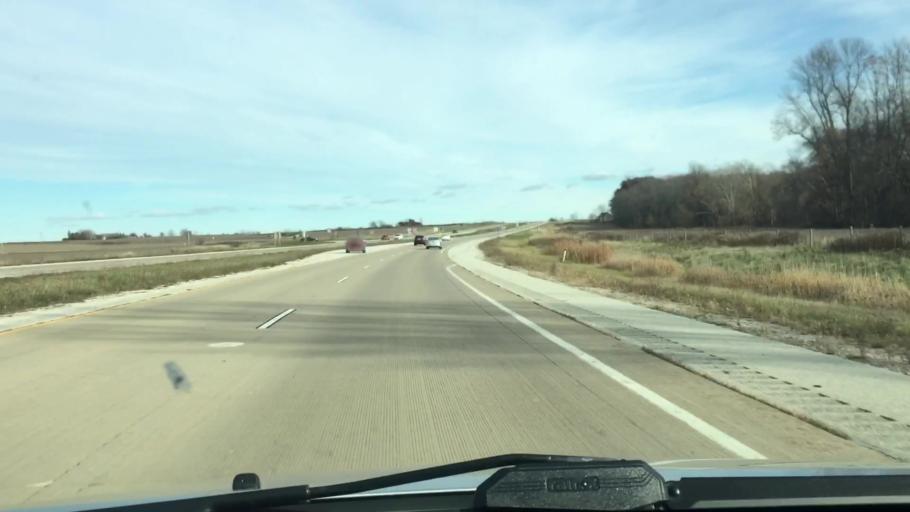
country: US
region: Wisconsin
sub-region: Kewaunee County
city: Luxemburg
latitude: 44.7167
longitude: -87.6740
